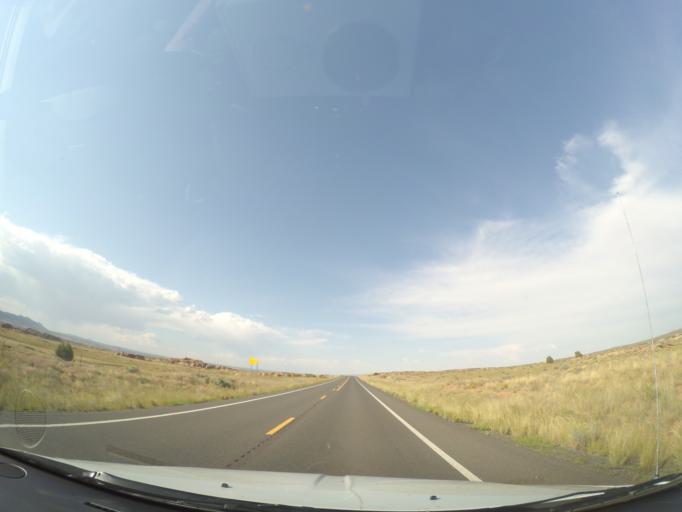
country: US
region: Arizona
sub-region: Coconino County
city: Tuba City
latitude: 36.3381
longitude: -111.4300
